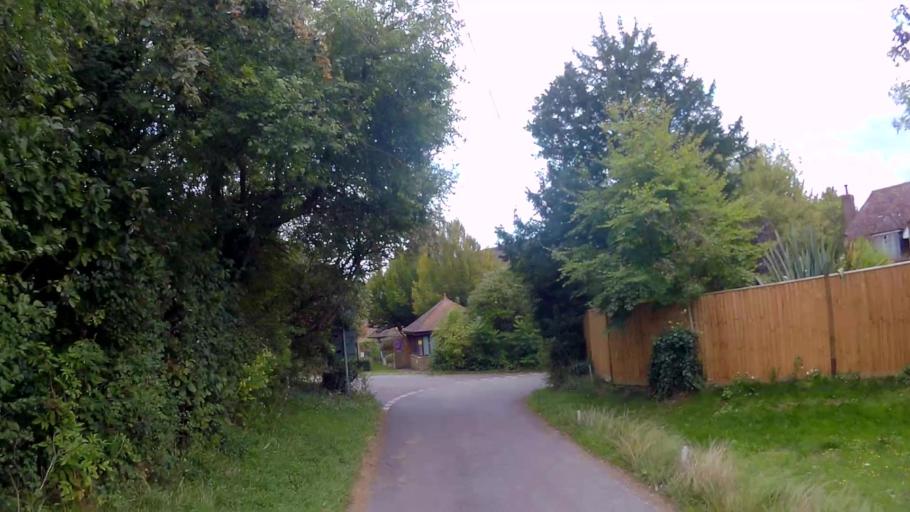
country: GB
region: England
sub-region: Hampshire
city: Kings Worthy
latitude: 51.1673
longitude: -1.3306
